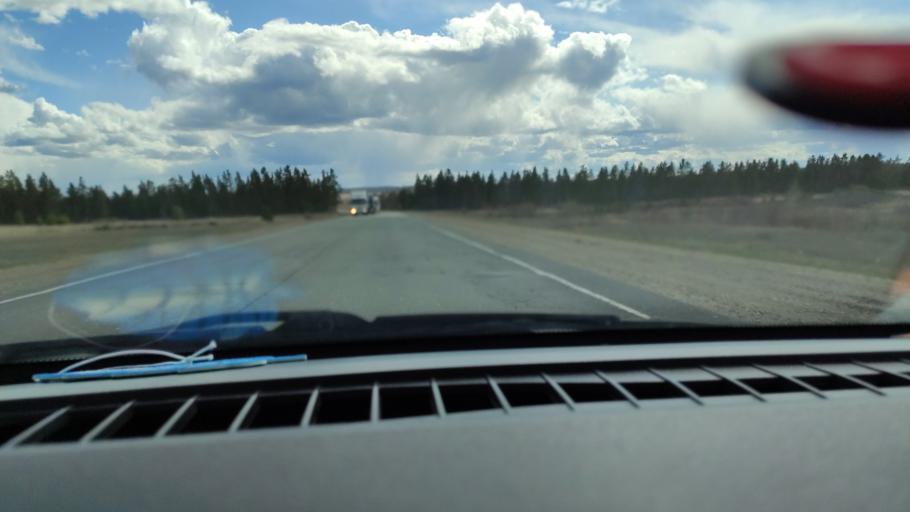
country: RU
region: Samara
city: Varlamovo
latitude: 53.1470
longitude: 48.2845
